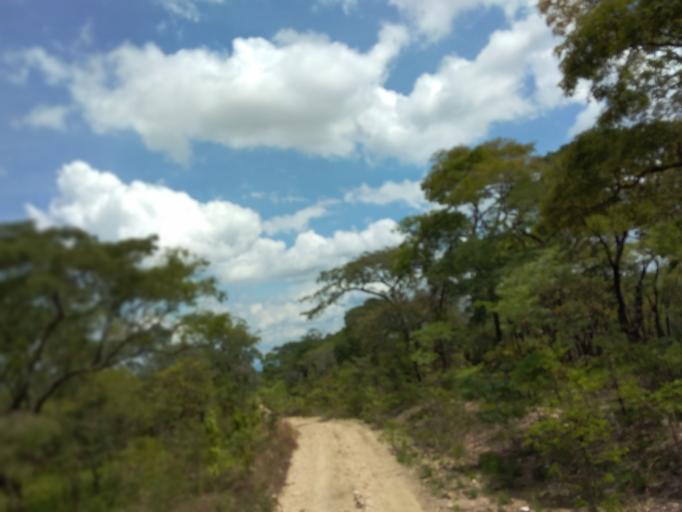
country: ZM
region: Central
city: Mkushi
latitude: -14.0730
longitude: 29.9632
